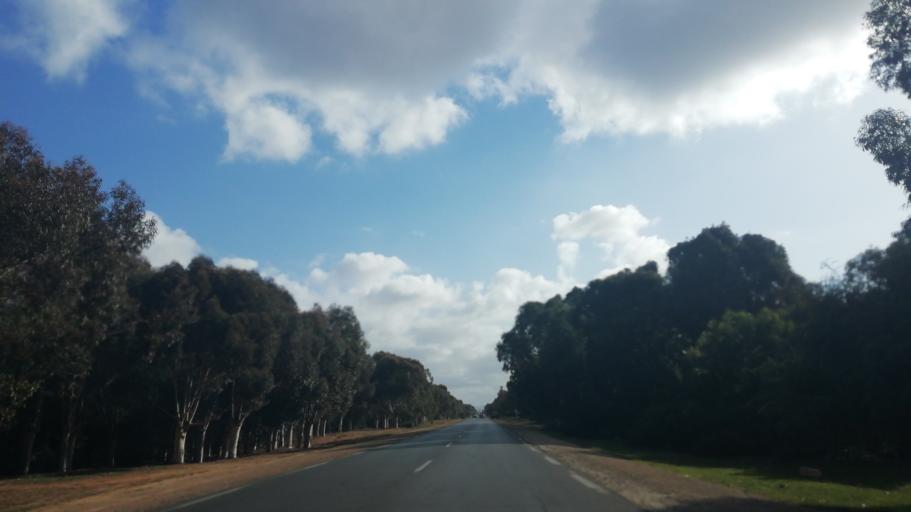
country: DZ
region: Relizane
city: Mazouna
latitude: 36.2499
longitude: 0.5534
